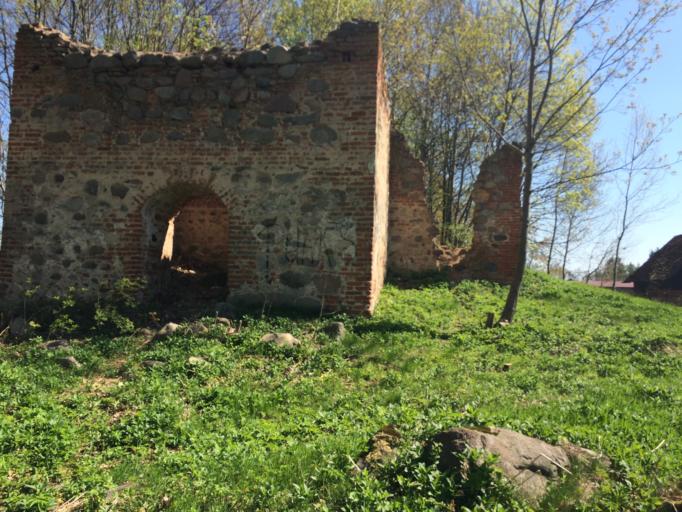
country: PL
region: Warmian-Masurian Voivodeship
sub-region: Powiat dzialdowski
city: Rybno
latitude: 53.3248
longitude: 19.9708
